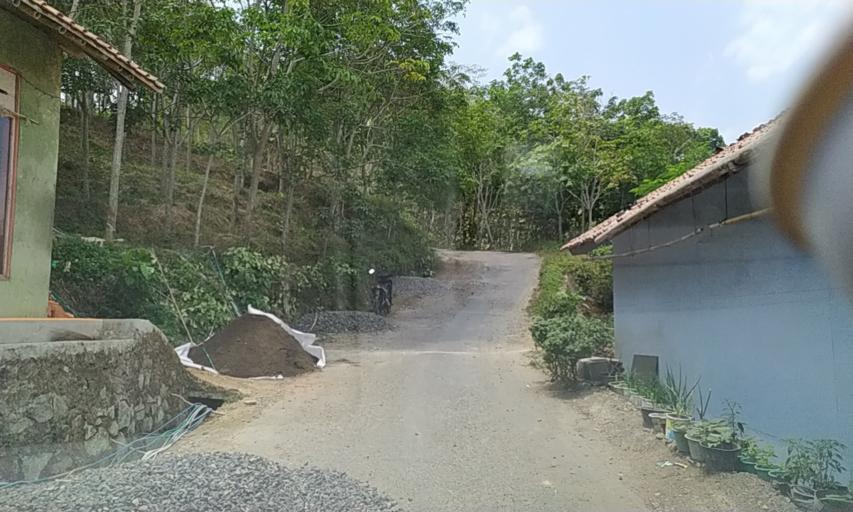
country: ID
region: Central Java
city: Jambuluwuk
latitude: -7.3316
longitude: 108.9280
